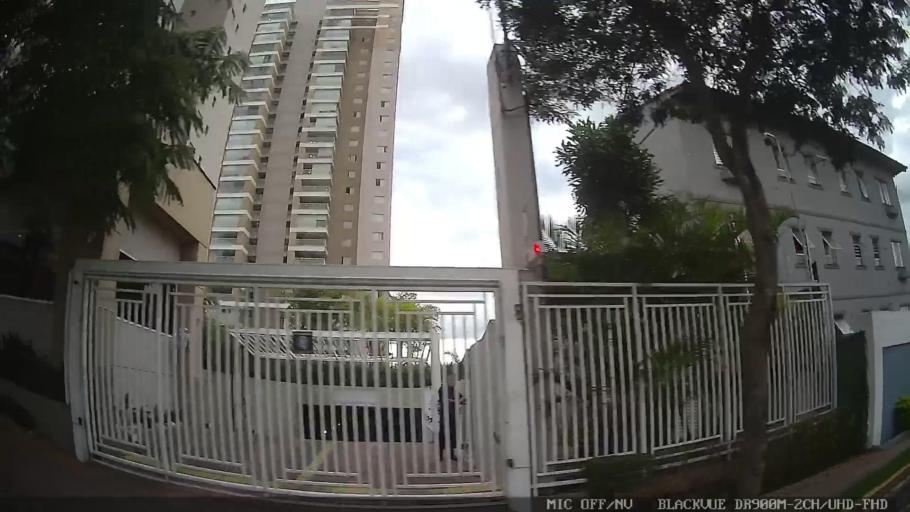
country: BR
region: Sao Paulo
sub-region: Mogi das Cruzes
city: Mogi das Cruzes
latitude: -23.5426
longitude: -46.1982
